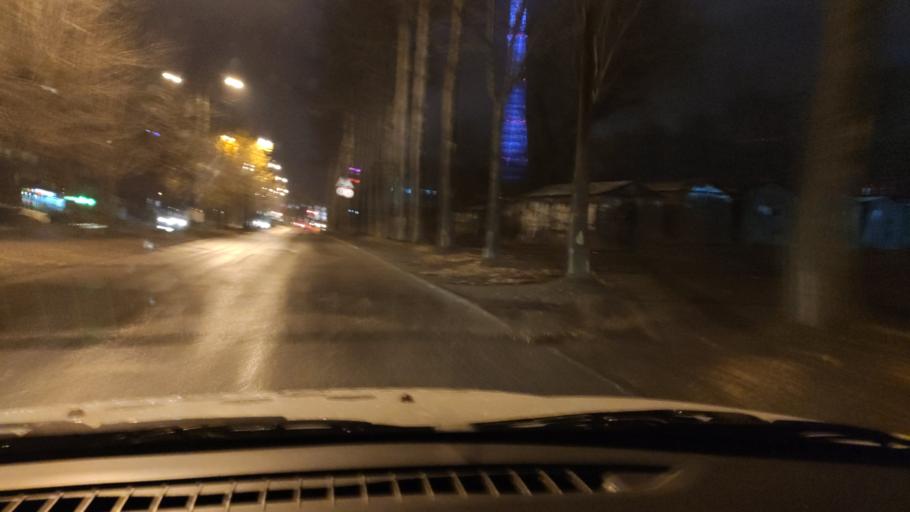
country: RU
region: Perm
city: Perm
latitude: 58.0122
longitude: 56.2936
